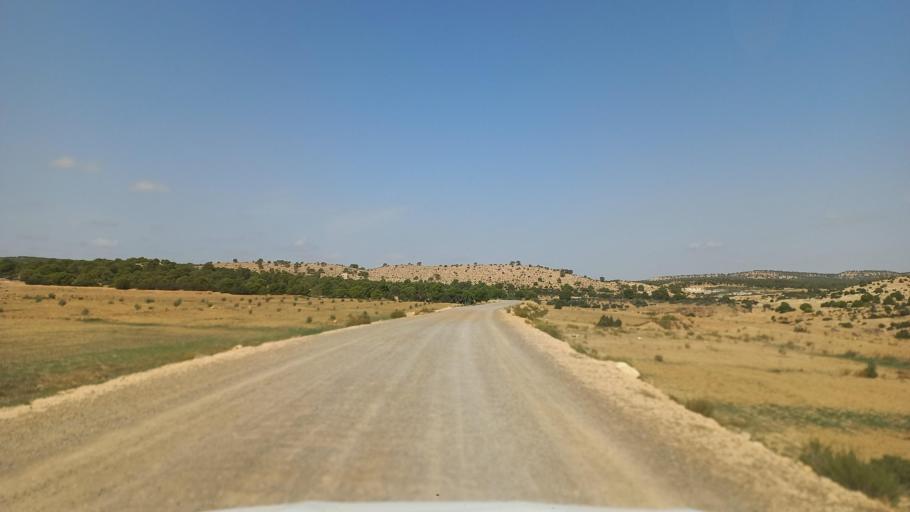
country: TN
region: Al Qasrayn
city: Sbiba
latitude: 35.3910
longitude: 8.9524
